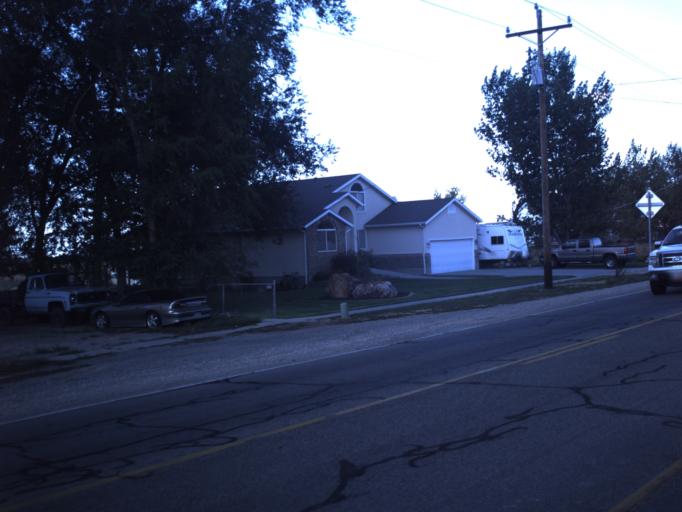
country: US
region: Utah
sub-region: Tooele County
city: Grantsville
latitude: 40.5996
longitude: -112.4307
